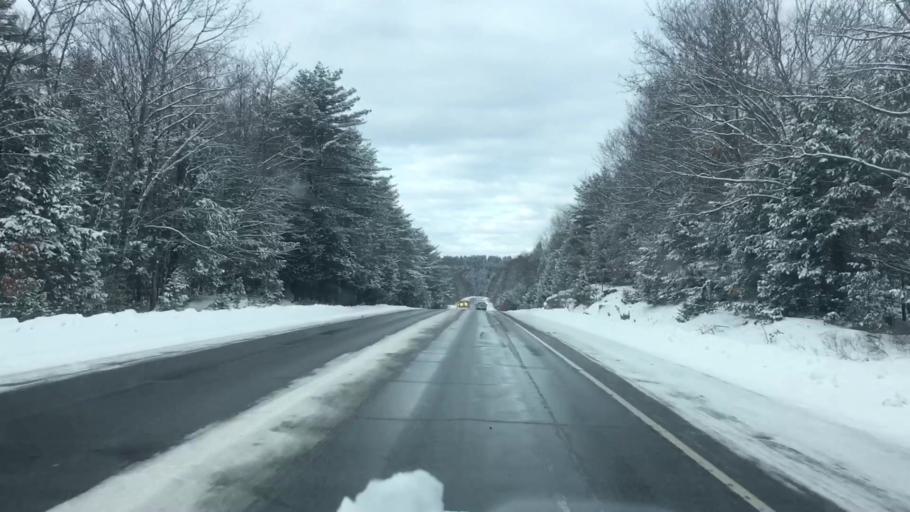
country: US
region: Maine
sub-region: Cumberland County
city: Bridgton
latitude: 44.0038
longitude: -70.6683
